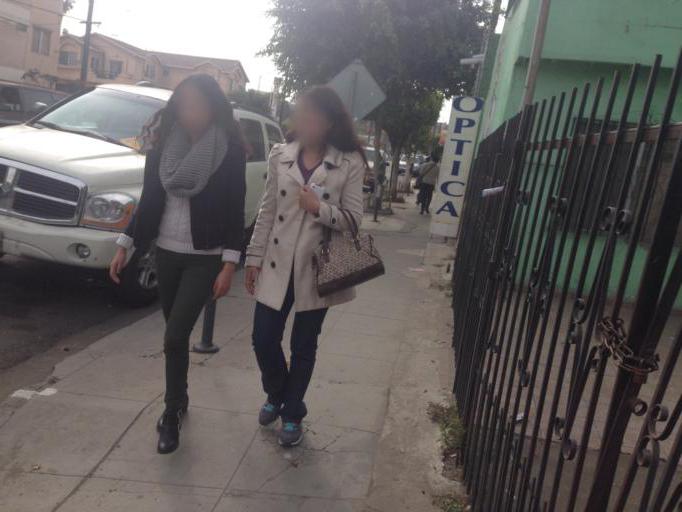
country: MX
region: Baja California
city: Tijuana
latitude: 32.5307
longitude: -117.0407
